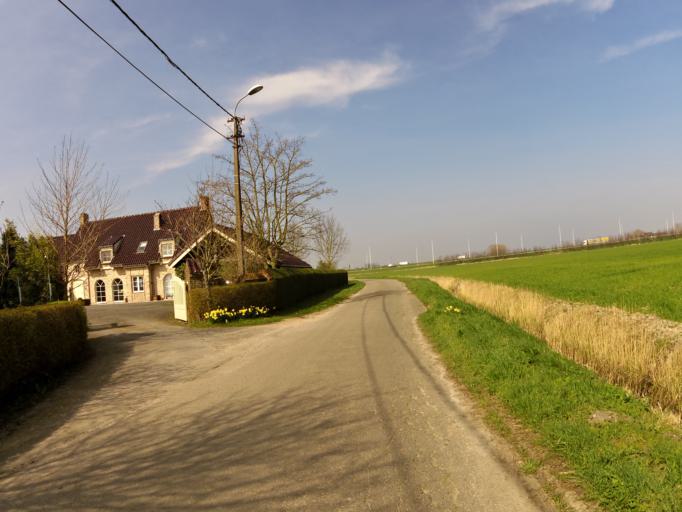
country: BE
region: Flanders
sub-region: Provincie West-Vlaanderen
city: Oudenburg
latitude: 51.1709
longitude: 3.0013
